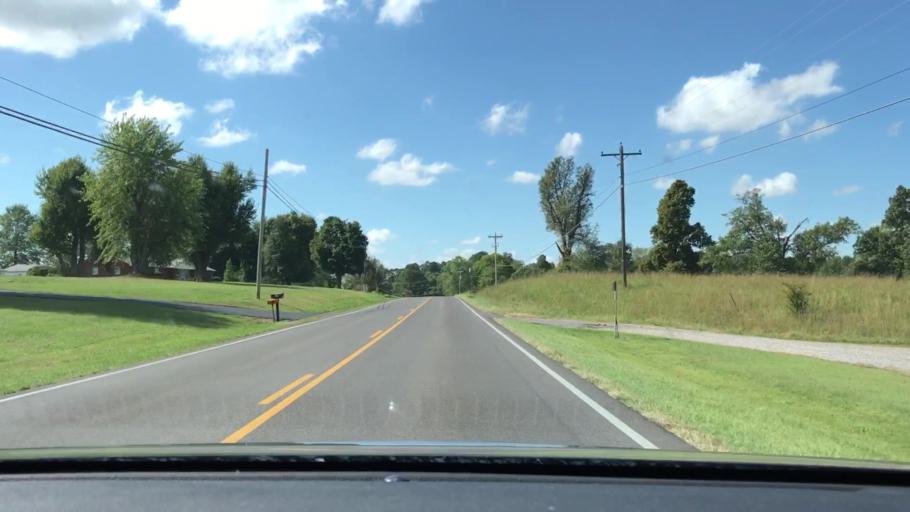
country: US
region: Kentucky
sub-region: Graves County
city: Mayfield
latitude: 36.7584
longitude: -88.6006
